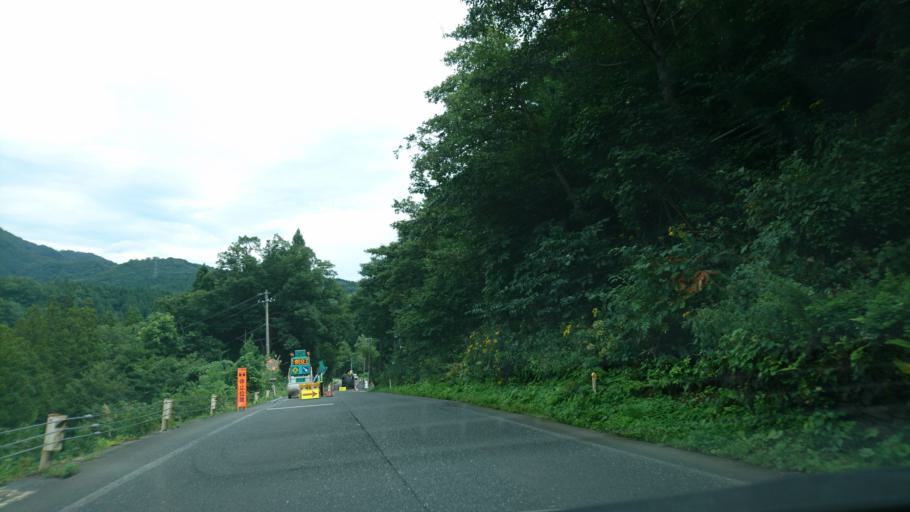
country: JP
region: Yamagata
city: Obanazawa
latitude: 38.8265
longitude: 140.6379
